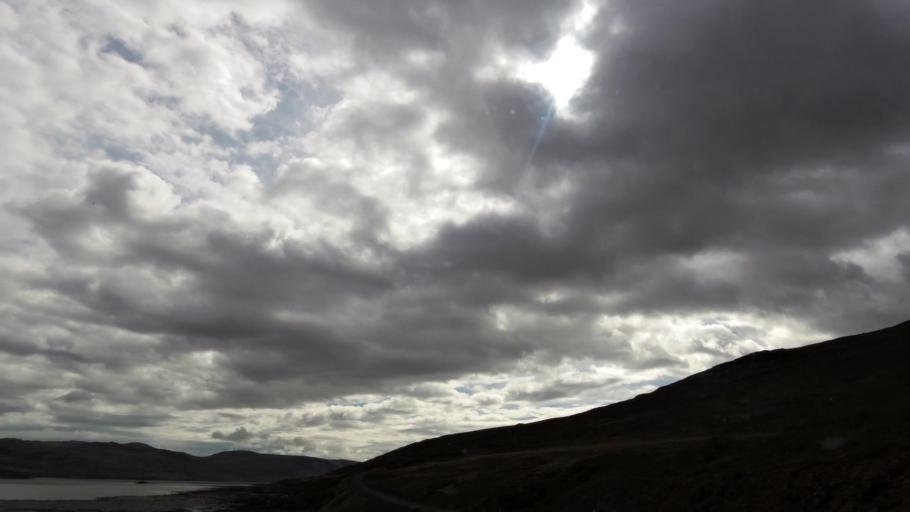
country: IS
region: West
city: Stykkisholmur
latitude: 65.5889
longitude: -22.1497
